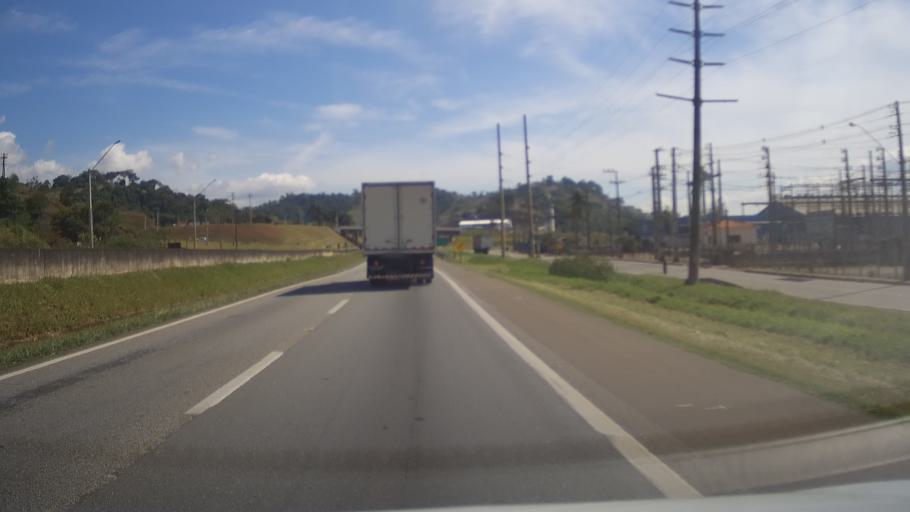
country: BR
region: Minas Gerais
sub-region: Cambui
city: Cambui
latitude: -22.5974
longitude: -46.0568
